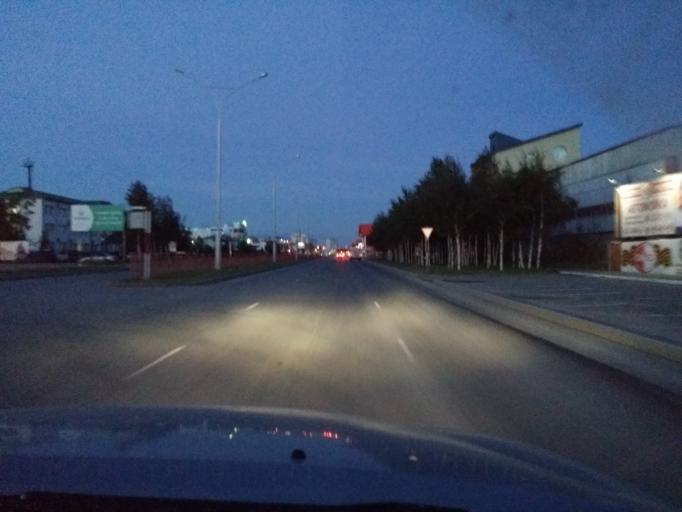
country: RU
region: Khanty-Mansiyskiy Avtonomnyy Okrug
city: Nizhnevartovsk
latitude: 60.9389
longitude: 76.5363
